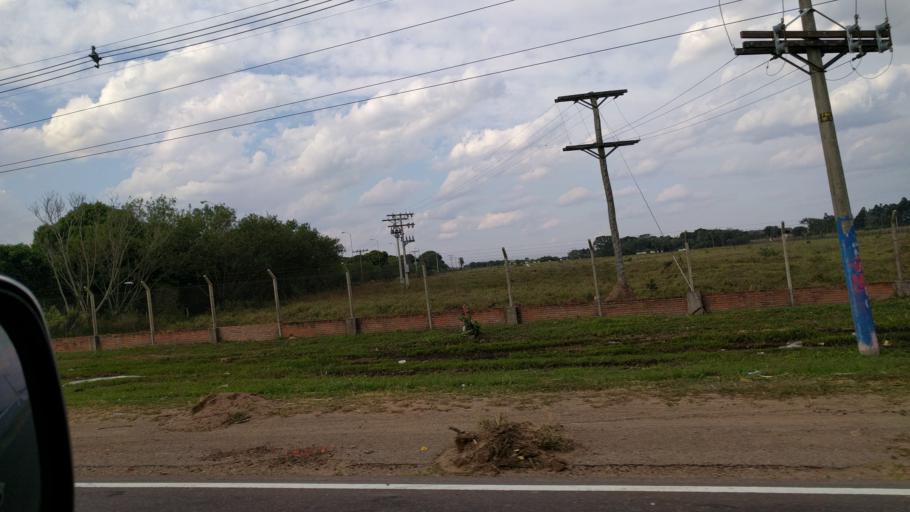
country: BO
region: Santa Cruz
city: La Belgica
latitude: -17.5573
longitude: -63.1595
